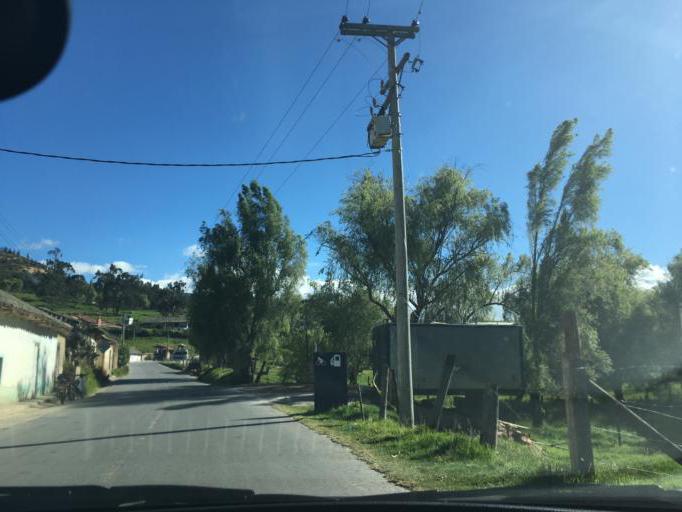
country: CO
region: Boyaca
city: Firavitoba
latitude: 5.6036
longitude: -72.9798
